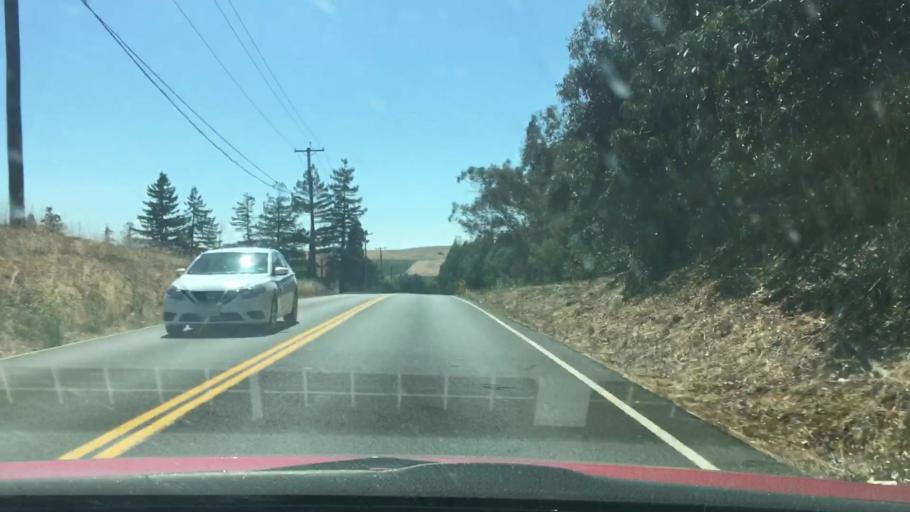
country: US
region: California
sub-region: Napa County
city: Napa
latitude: 38.2742
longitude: -122.3272
